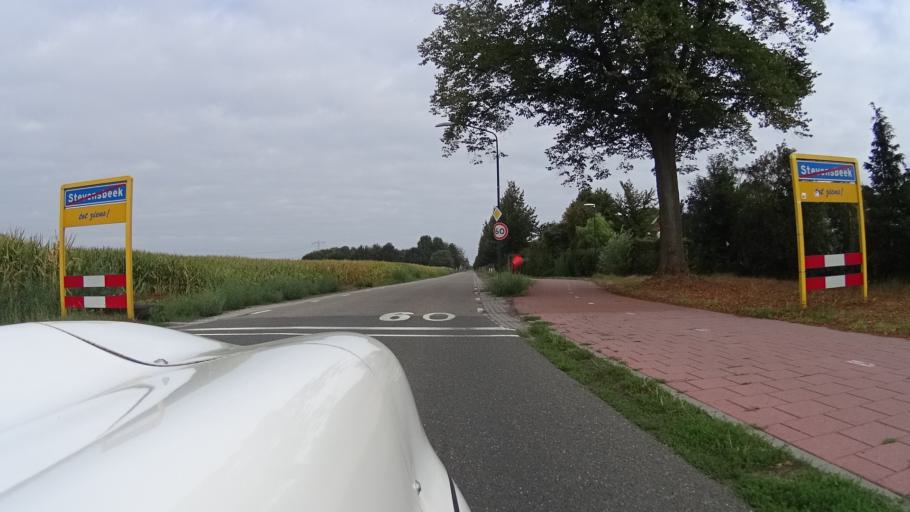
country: NL
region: North Brabant
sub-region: Gemeente Sint Anthonis
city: Sint Anthonis
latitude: 51.6050
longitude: 5.9137
